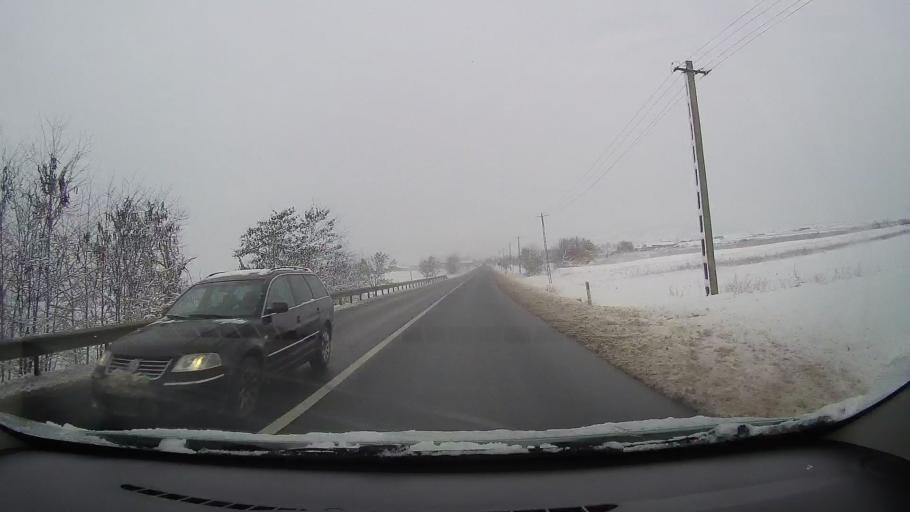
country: RO
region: Alba
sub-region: Municipiul Sebes
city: Lancram
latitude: 45.9848
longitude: 23.5116
